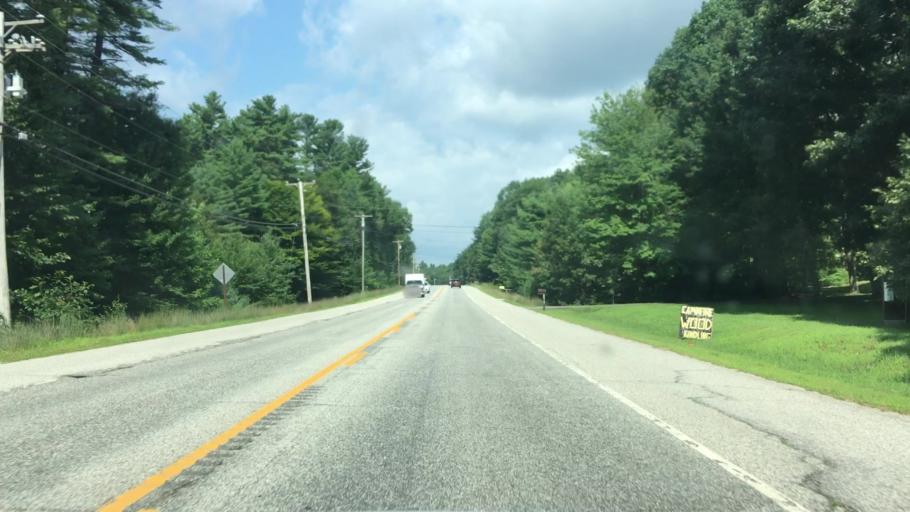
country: US
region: Maine
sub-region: Cumberland County
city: Raymond
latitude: 43.9037
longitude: -70.4827
